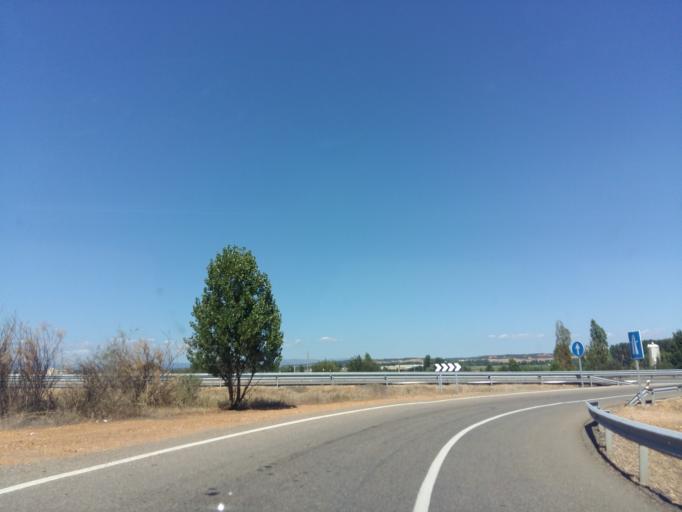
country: ES
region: Castille and Leon
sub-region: Provincia de Leon
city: Astorga
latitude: 42.4383
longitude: -6.0393
